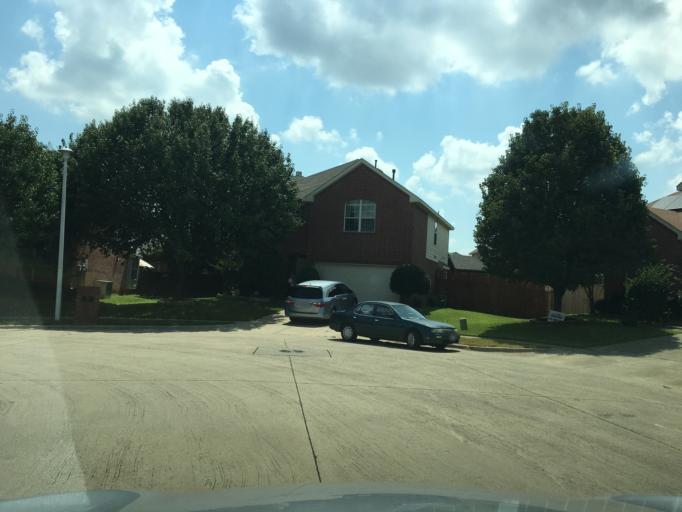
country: US
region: Texas
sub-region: Dallas County
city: Garland
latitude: 32.9500
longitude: -96.6437
